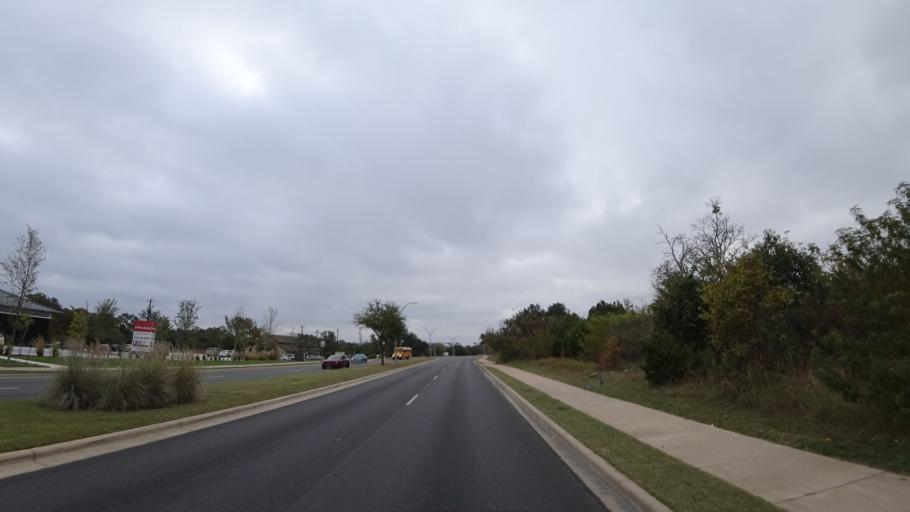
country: US
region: Texas
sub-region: Williamson County
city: Cedar Park
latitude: 30.5040
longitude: -97.8483
